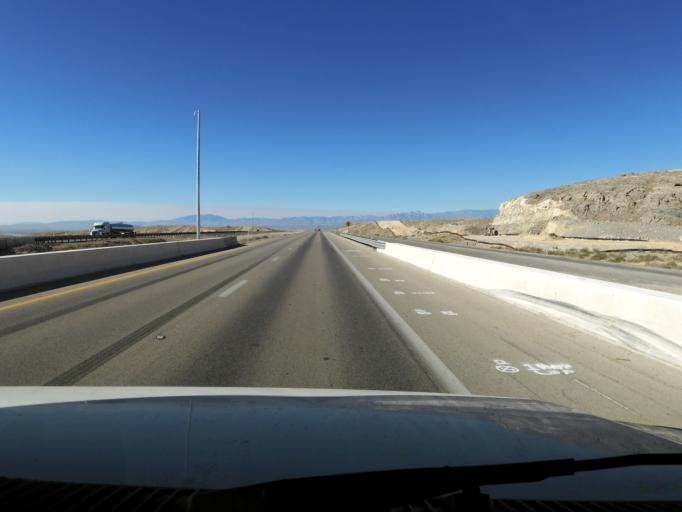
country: US
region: Nevada
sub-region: Clark County
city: Nellis Air Force Base
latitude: 36.3108
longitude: -114.9532
